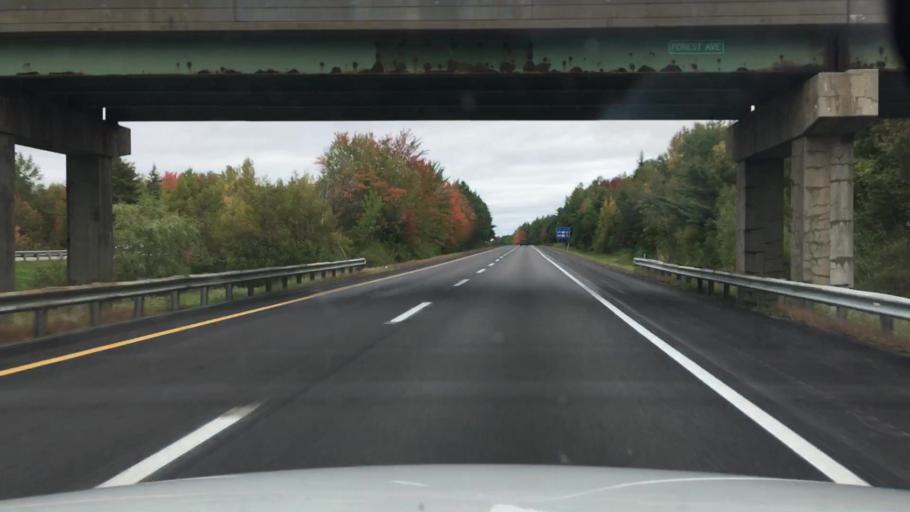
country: US
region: Maine
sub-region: Penobscot County
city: Orono
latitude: 44.8895
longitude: -68.6934
